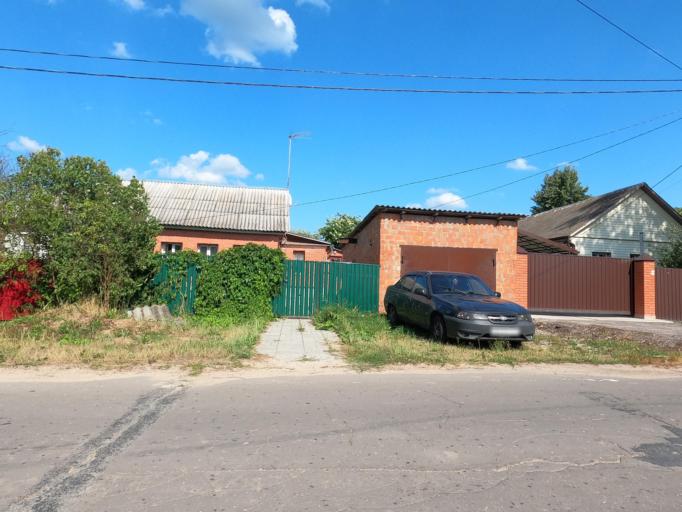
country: RU
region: Moskovskaya
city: Peski
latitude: 55.2273
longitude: 38.7505
